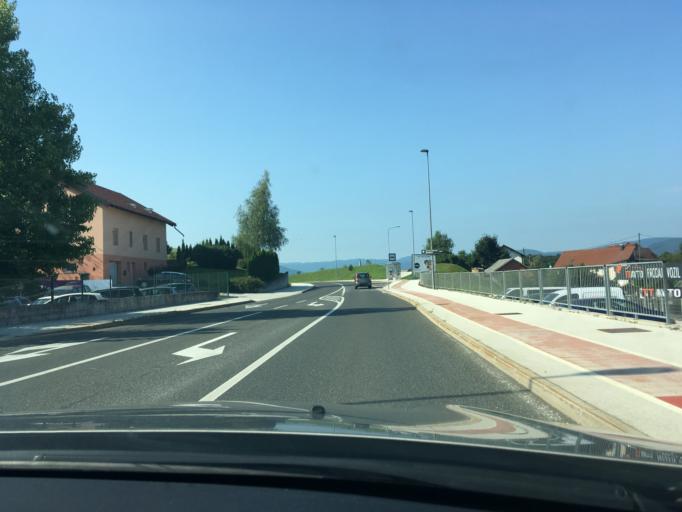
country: SI
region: Novo Mesto
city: Novo Mesto
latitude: 45.8282
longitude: 15.1567
